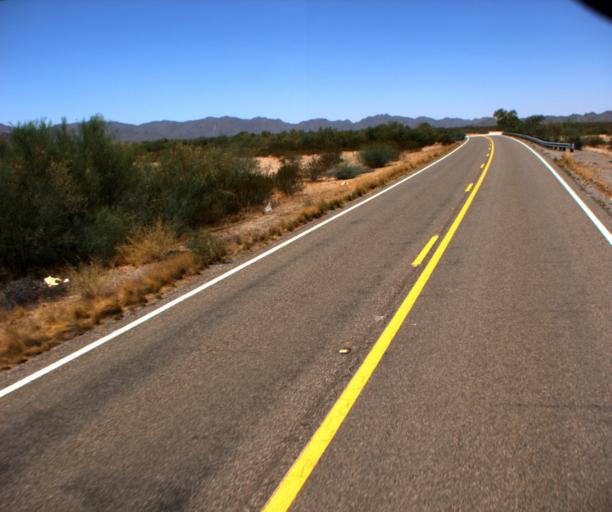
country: US
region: Arizona
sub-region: Pinal County
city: Maricopa
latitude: 33.0309
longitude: -112.3639
